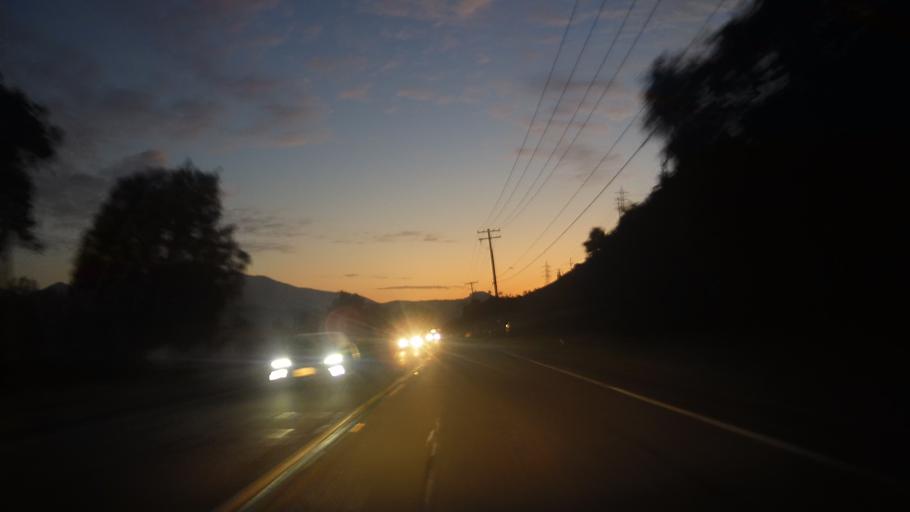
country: US
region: California
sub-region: San Diego County
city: Rancho San Diego
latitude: 32.7542
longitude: -116.9055
